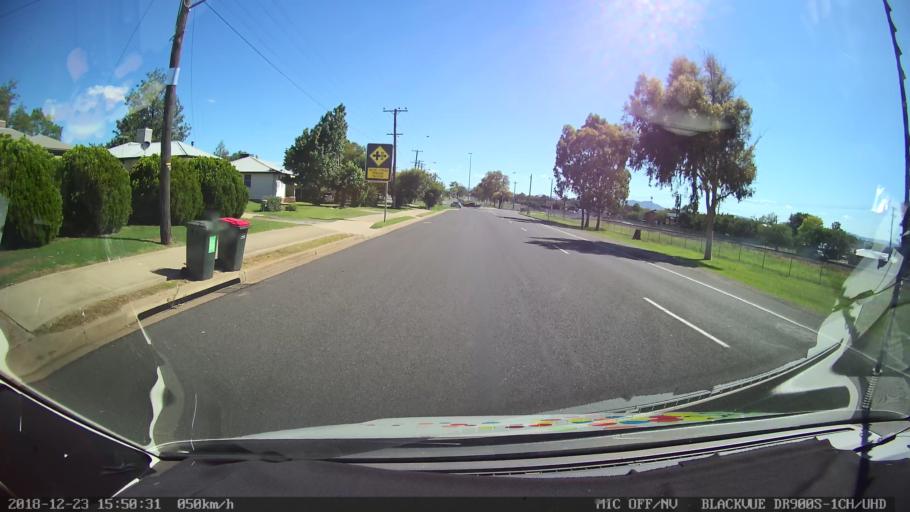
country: AU
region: New South Wales
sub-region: Tamworth Municipality
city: South Tamworth
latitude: -31.1067
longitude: 150.9003
